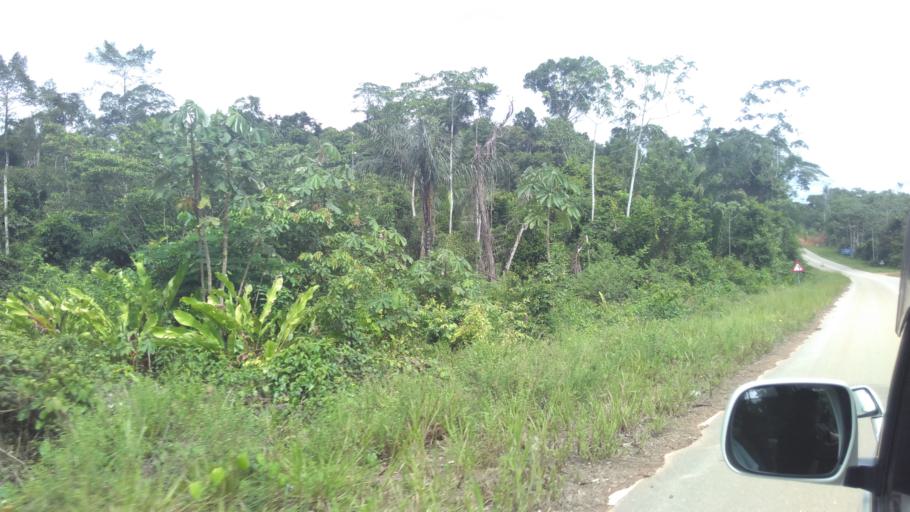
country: SR
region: Brokopondo
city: Brownsweg
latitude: 4.5506
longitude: -55.3714
